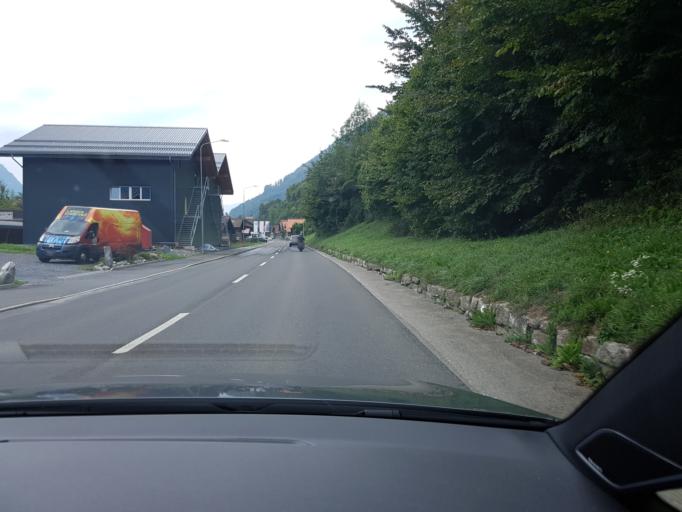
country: CH
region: Bern
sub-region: Interlaken-Oberhasli District
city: Ringgenberg
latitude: 46.7068
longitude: 7.9064
